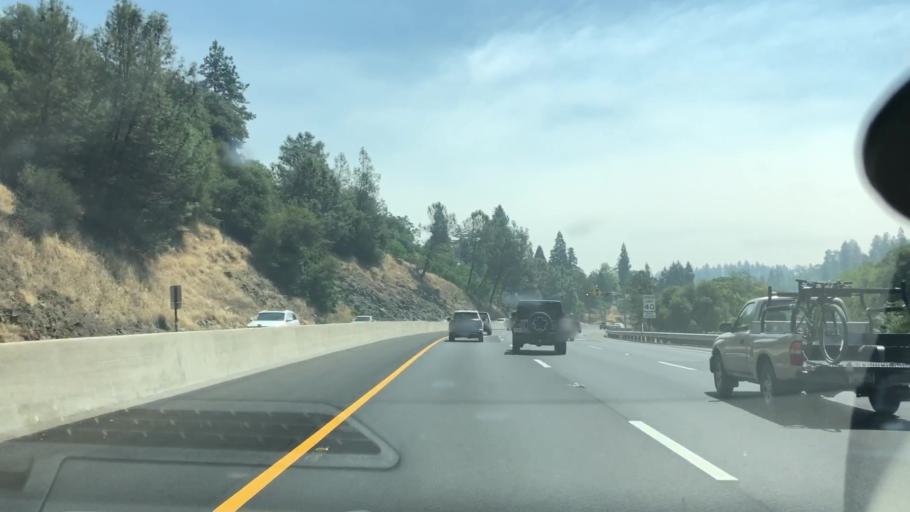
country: US
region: California
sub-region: El Dorado County
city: Placerville
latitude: 38.7298
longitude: -120.8122
